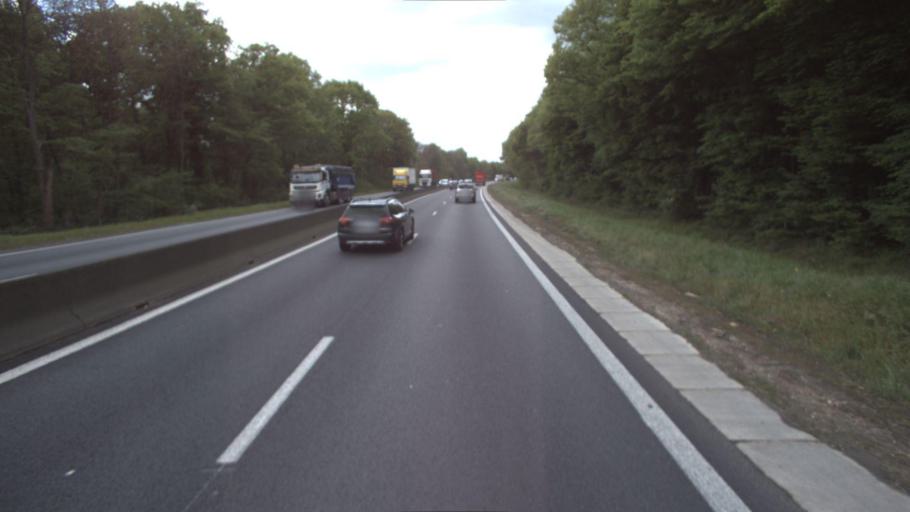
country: FR
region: Ile-de-France
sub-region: Departement de Seine-et-Marne
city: Gretz-Armainvilliers
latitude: 48.7333
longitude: 2.7209
